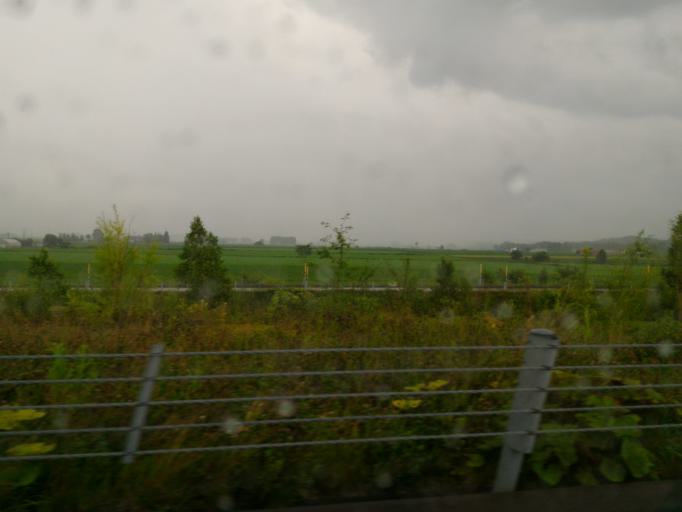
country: JP
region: Hokkaido
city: Nayoro
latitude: 44.4423
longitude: 142.3706
